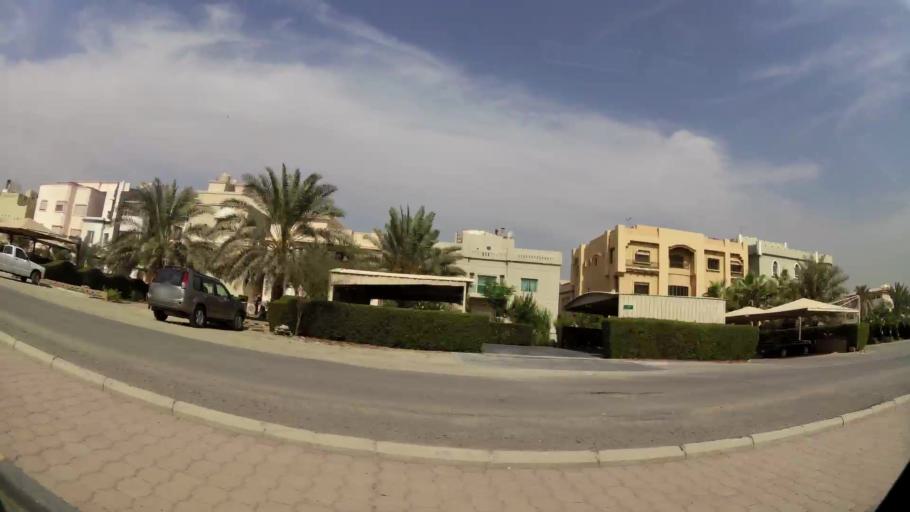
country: KW
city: Bayan
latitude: 29.2771
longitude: 48.0235
